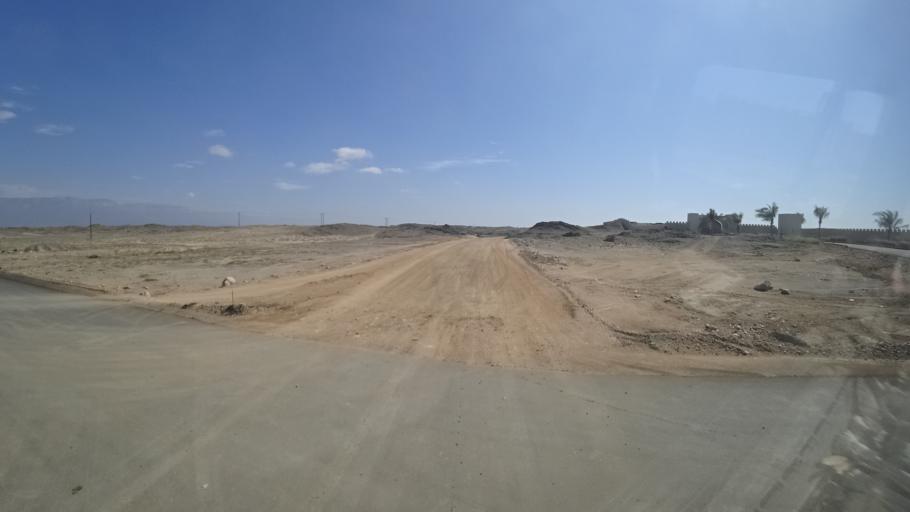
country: OM
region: Zufar
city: Salalah
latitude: 16.9637
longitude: 54.7739
